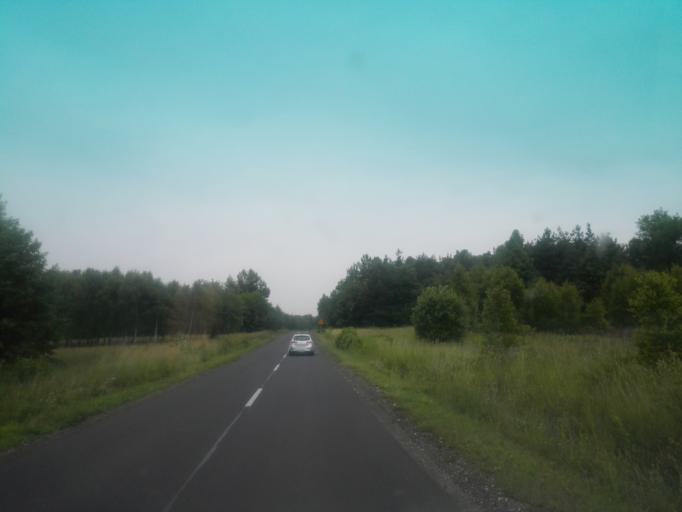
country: PL
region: Silesian Voivodeship
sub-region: Powiat czestochowski
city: Olsztyn
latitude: 50.7853
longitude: 19.2731
